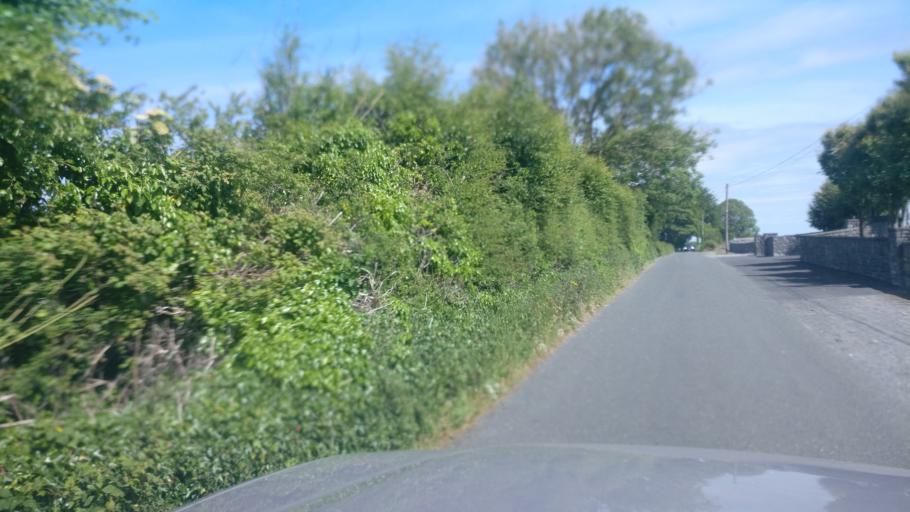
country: IE
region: Connaught
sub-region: County Galway
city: Gort
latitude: 53.1201
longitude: -8.7913
